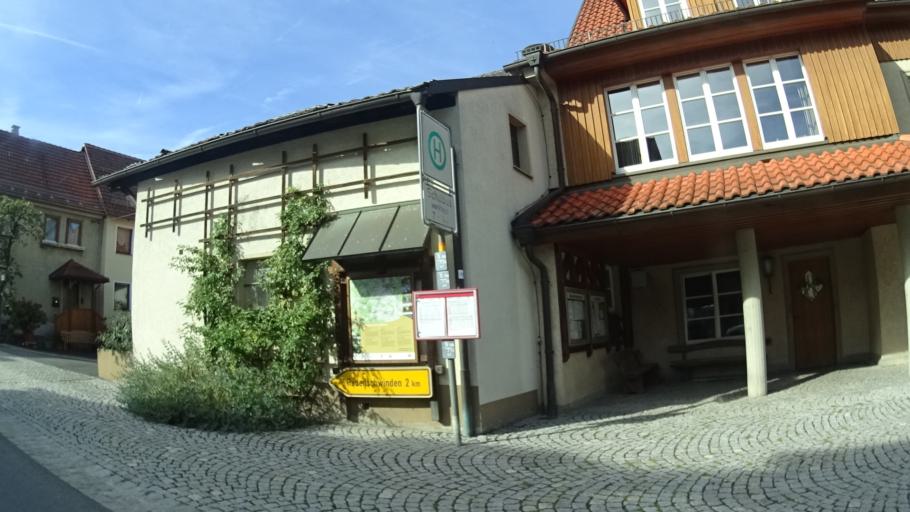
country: DE
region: Bavaria
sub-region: Regierungsbezirk Unterfranken
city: Hausen
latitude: 50.5055
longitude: 10.1281
